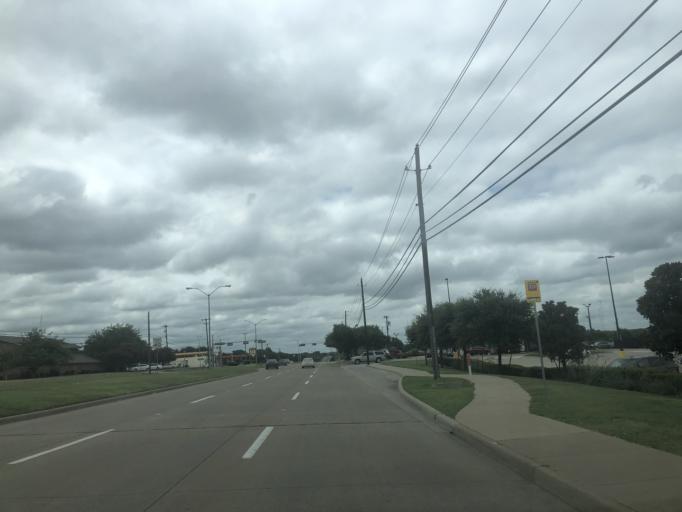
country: US
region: Texas
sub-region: Dallas County
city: Duncanville
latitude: 32.6489
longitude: -96.9431
